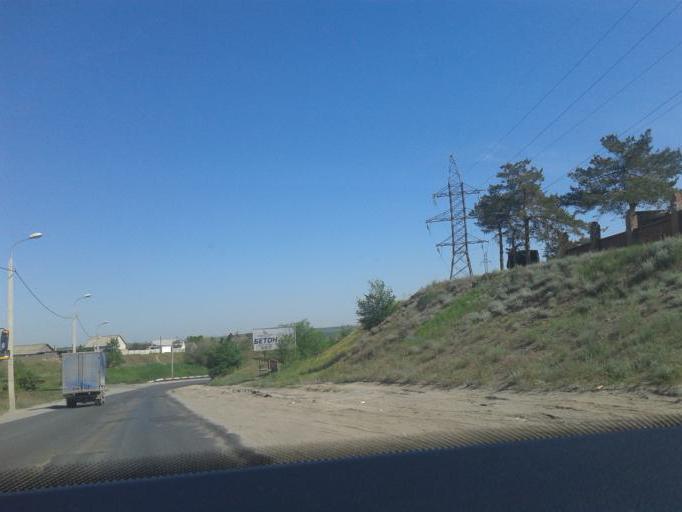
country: RU
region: Volgograd
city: Volgograd
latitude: 48.7053
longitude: 44.4418
